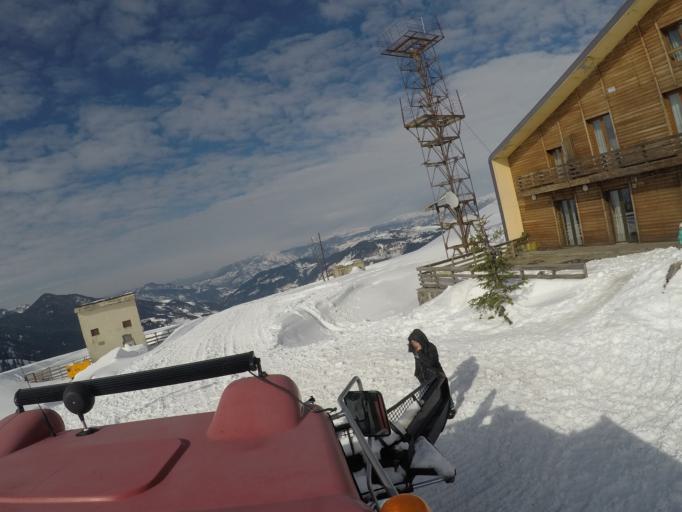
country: GE
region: Ajaria
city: Dioknisi
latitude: 41.6342
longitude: 42.5103
